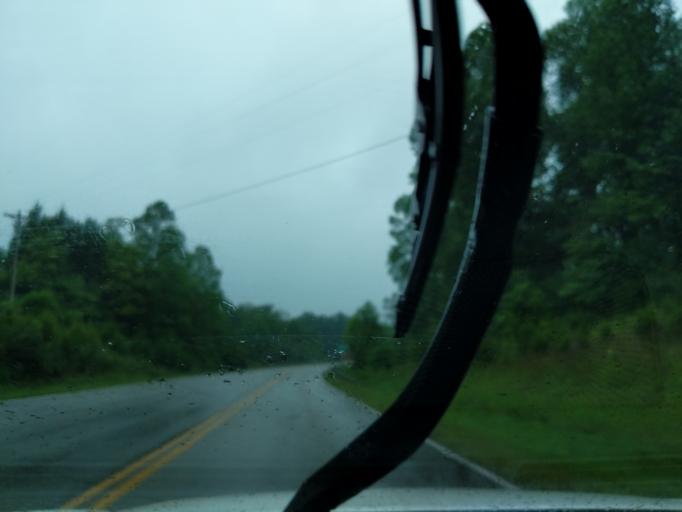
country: US
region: Kentucky
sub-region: Barren County
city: Cave City
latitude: 37.1289
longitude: -86.0639
